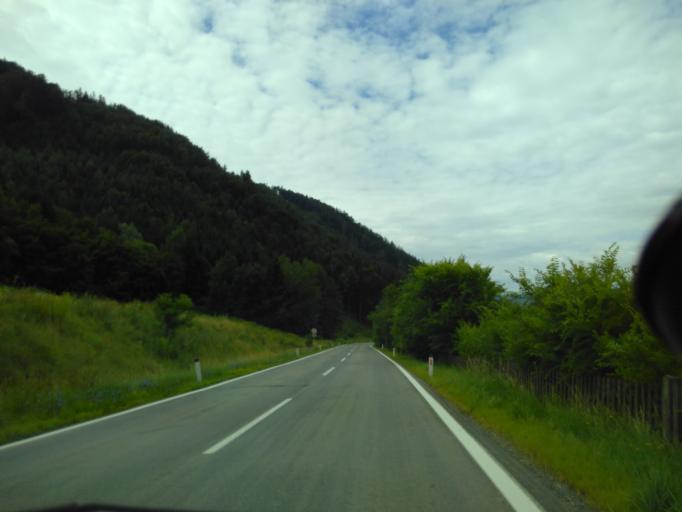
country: AT
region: Styria
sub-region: Politischer Bezirk Graz-Umgebung
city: Schrems bei Frohnleiten
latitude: 47.2764
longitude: 15.3506
